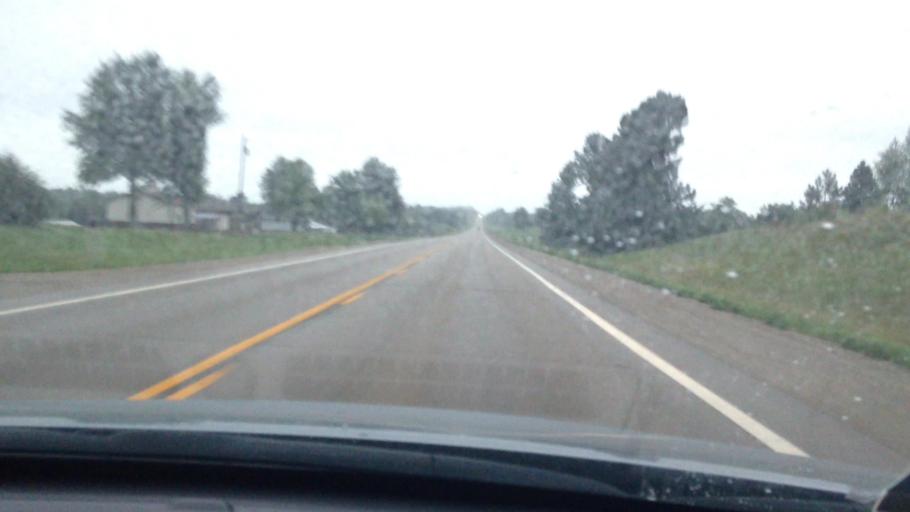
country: US
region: Kansas
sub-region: Brown County
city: Hiawatha
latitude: 39.8356
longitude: -95.5272
